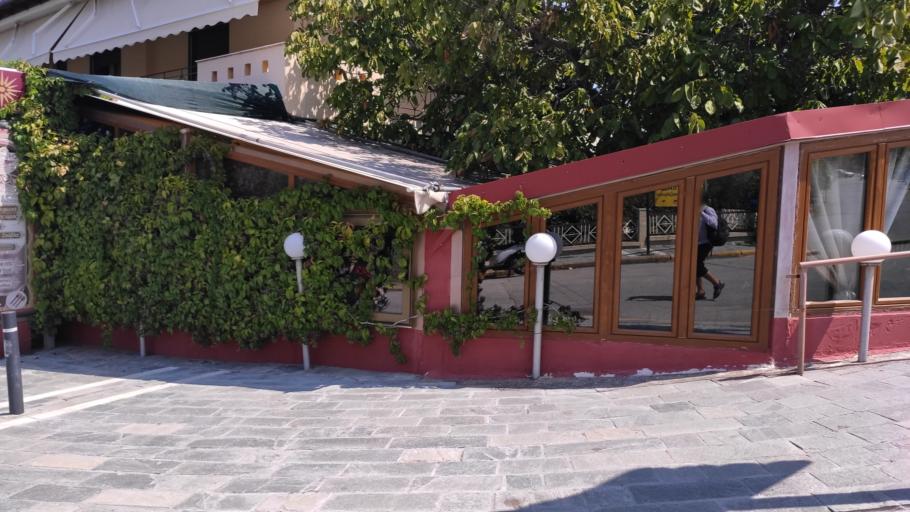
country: GR
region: Central Macedonia
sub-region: Nomos Imathias
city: Vergina
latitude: 40.4861
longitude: 22.3206
